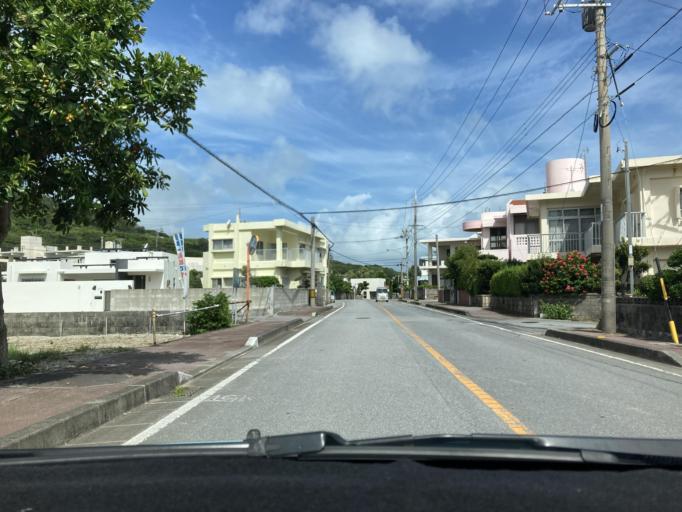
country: JP
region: Okinawa
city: Ginowan
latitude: 26.1827
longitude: 127.8191
